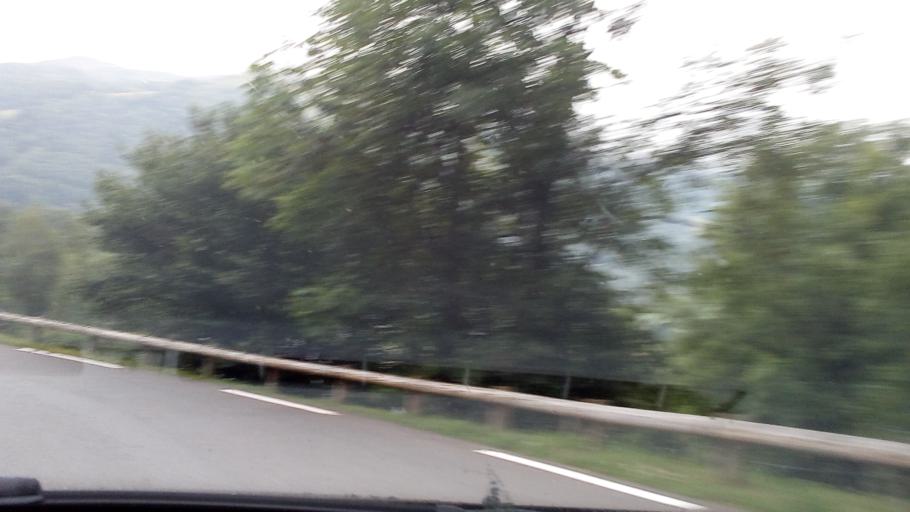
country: FR
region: Midi-Pyrenees
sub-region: Departement des Hautes-Pyrenees
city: Cauterets
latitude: 42.9610
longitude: -0.2205
